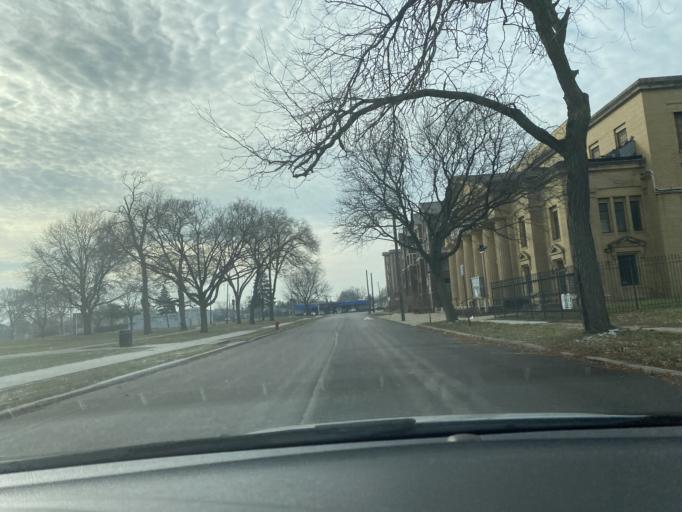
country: US
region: Michigan
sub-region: Wayne County
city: Highland Park
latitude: 42.3681
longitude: -83.1329
